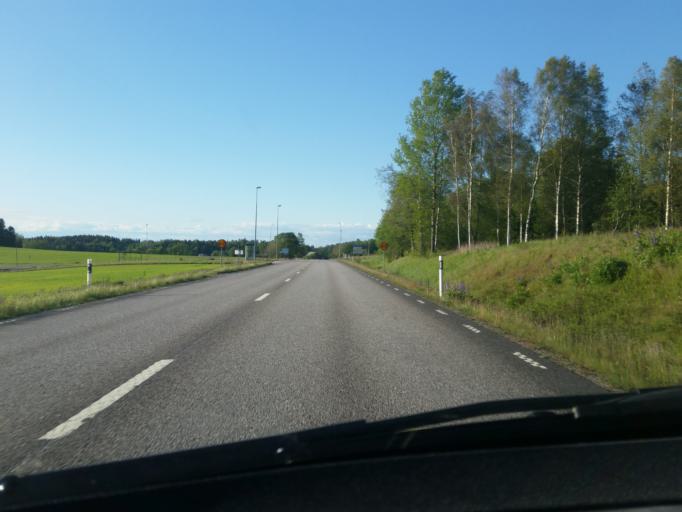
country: SE
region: Vaestra Goetaland
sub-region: Fargelanda Kommun
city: Faergelanda
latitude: 58.5410
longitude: 11.9878
